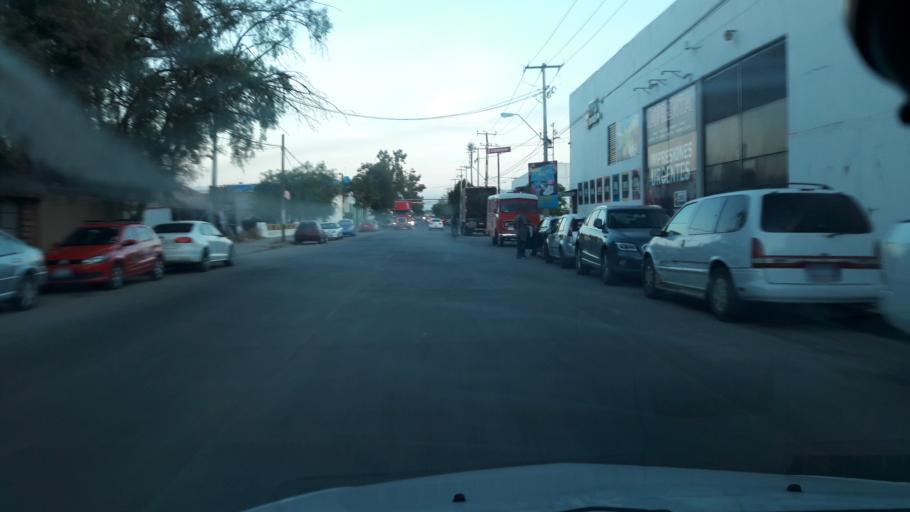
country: MX
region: Guanajuato
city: Leon
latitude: 21.1685
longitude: -101.6771
